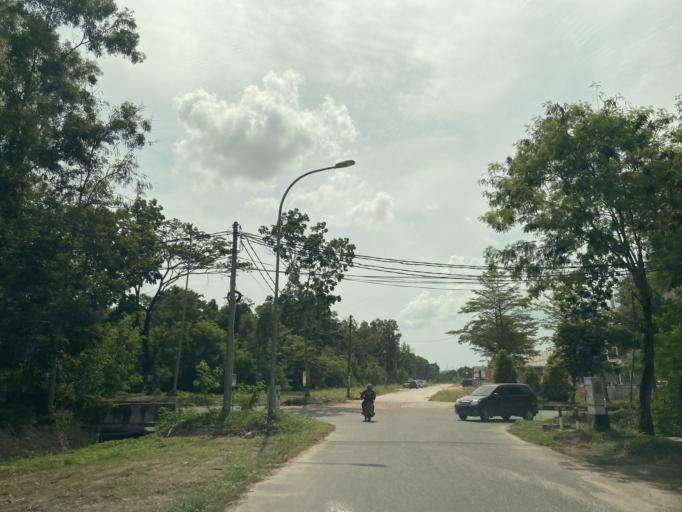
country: SG
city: Singapore
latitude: 1.1282
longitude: 104.0462
